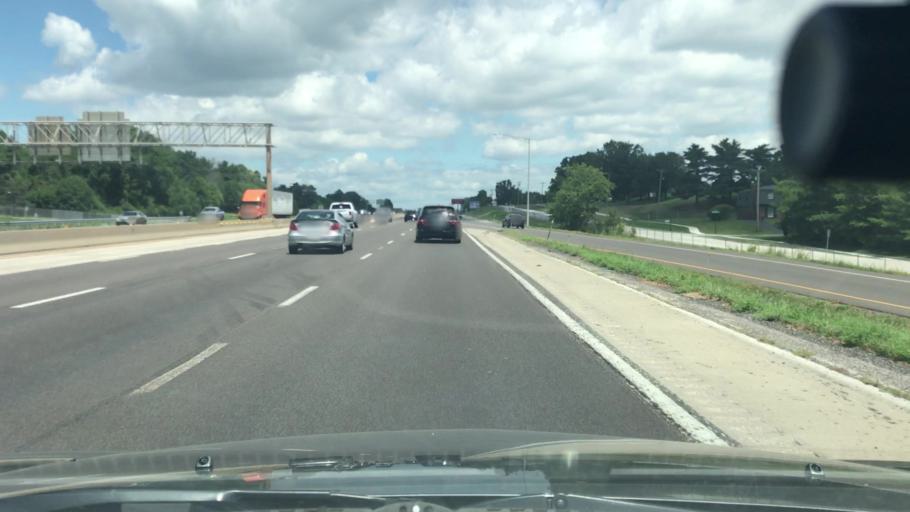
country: US
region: Missouri
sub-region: Saint Louis County
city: Creve Coeur
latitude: 38.6574
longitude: -90.4481
